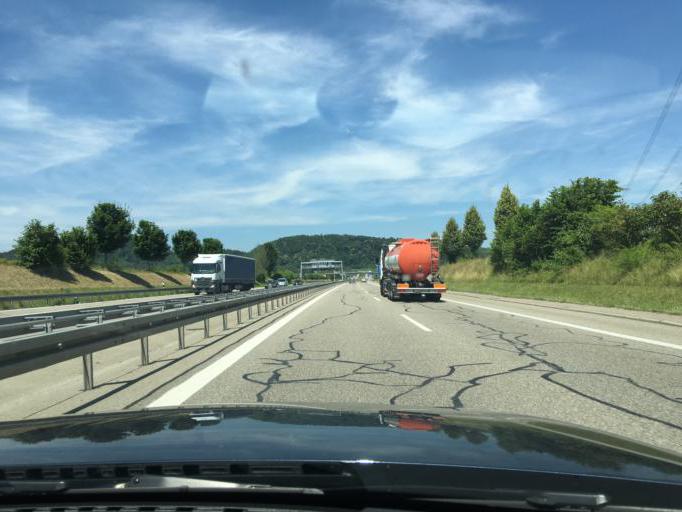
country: DE
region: Baden-Wuerttemberg
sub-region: Freiburg Region
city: Rheinfelden (Baden)
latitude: 47.5582
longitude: 7.7578
